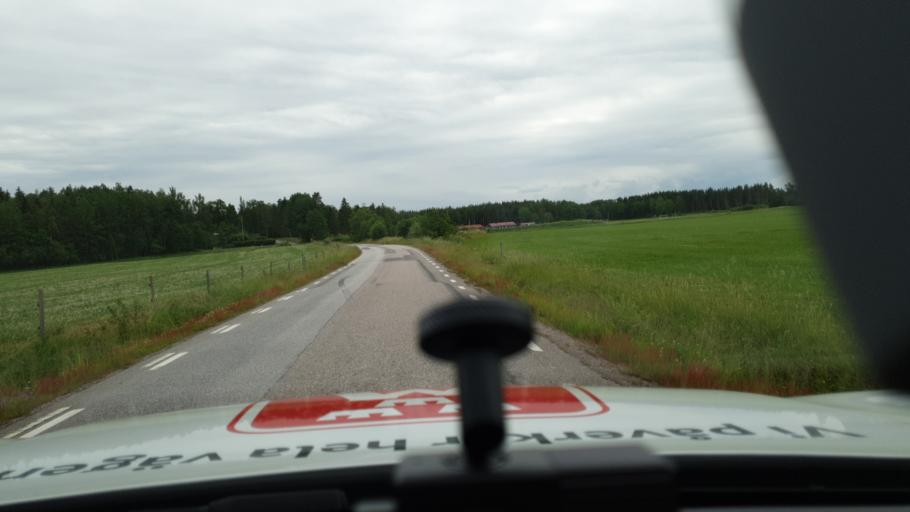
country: SE
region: Vaestra Goetaland
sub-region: Skovde Kommun
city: Stopen
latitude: 58.5735
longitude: 13.8491
